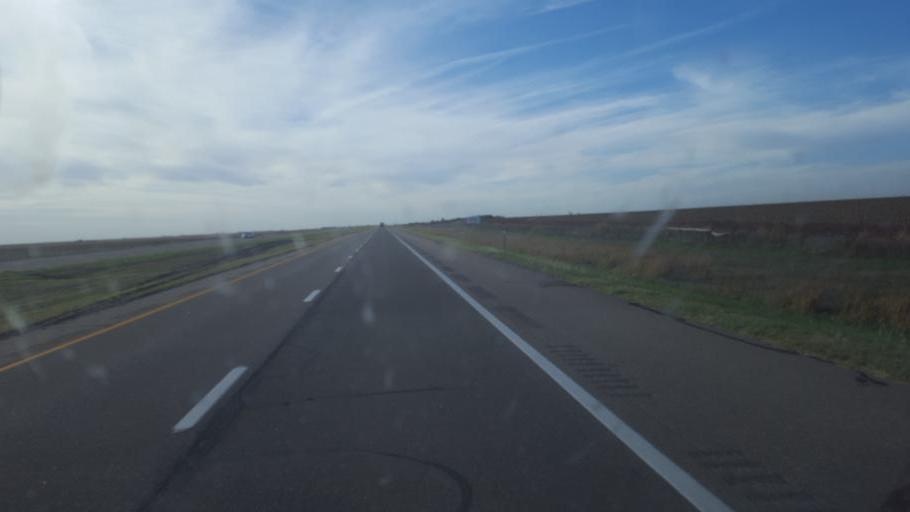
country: US
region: Kansas
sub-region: Gove County
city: Gove
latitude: 39.0349
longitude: -100.1924
